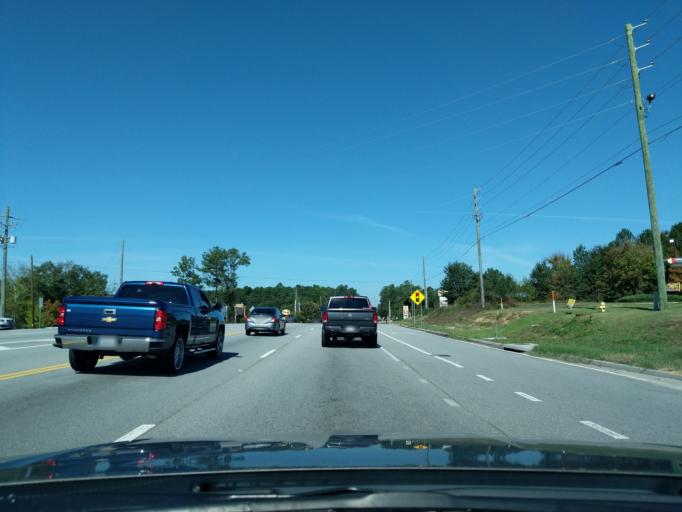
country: US
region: Georgia
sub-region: Richmond County
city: Augusta
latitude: 33.3670
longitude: -81.9961
